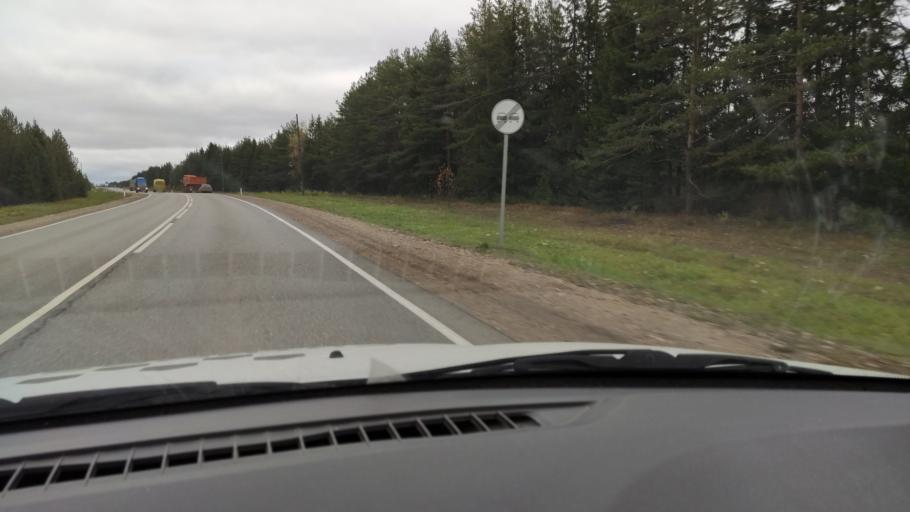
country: RU
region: Kirov
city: Slobodskoy
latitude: 58.7340
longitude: 50.2867
